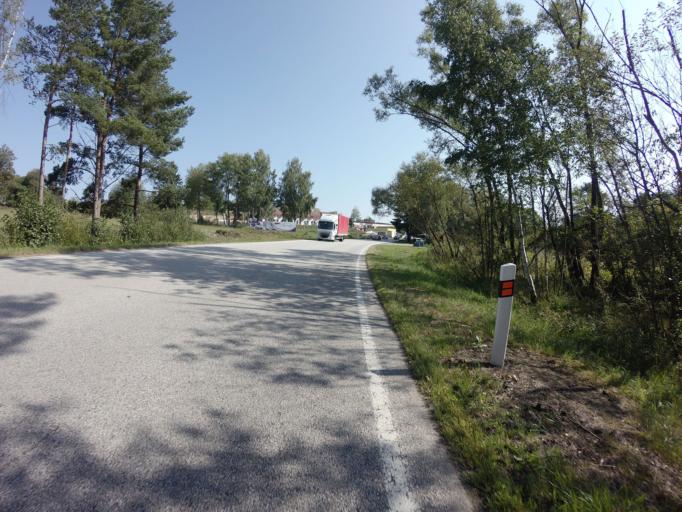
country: CZ
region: Jihocesky
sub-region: Okres Cesky Krumlov
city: Vyssi Brod
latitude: 48.5862
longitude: 14.3210
